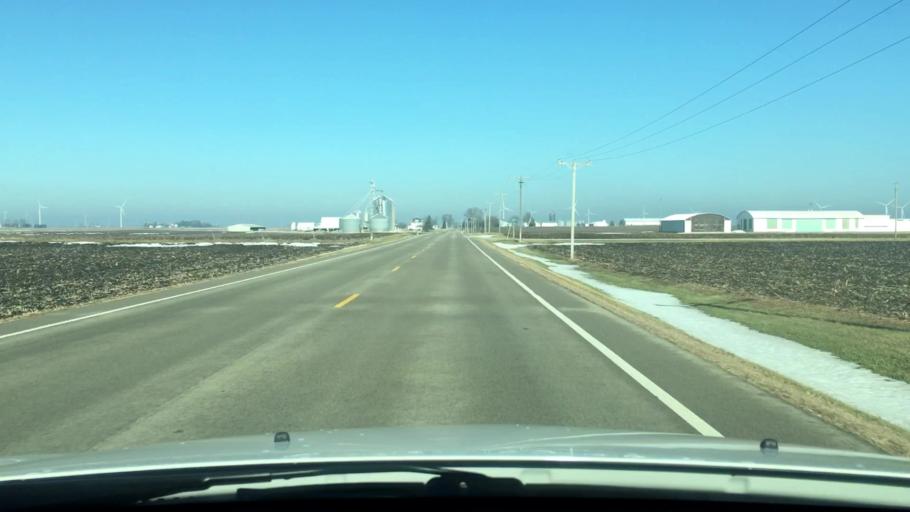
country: US
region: Illinois
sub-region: DeKalb County
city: Waterman
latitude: 41.7817
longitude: -88.8772
